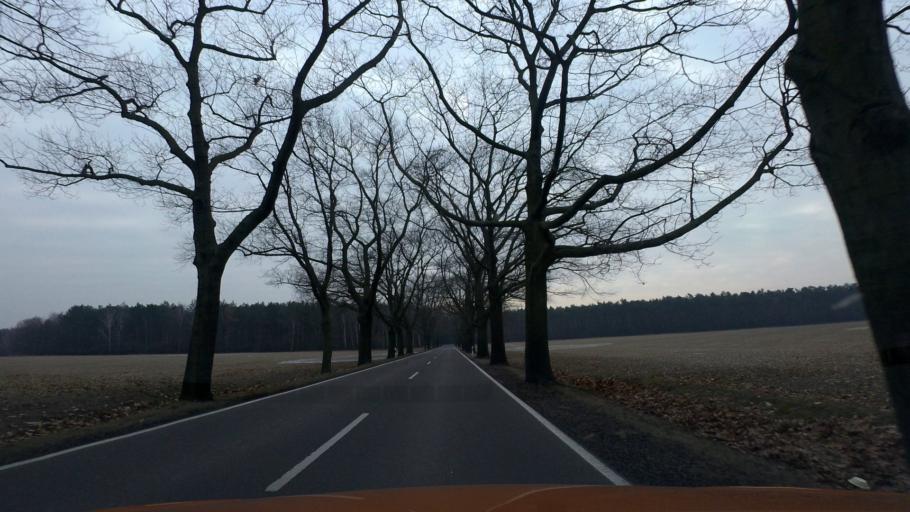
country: DE
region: Brandenburg
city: Ludwigsfelde
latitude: 52.2739
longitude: 13.2179
